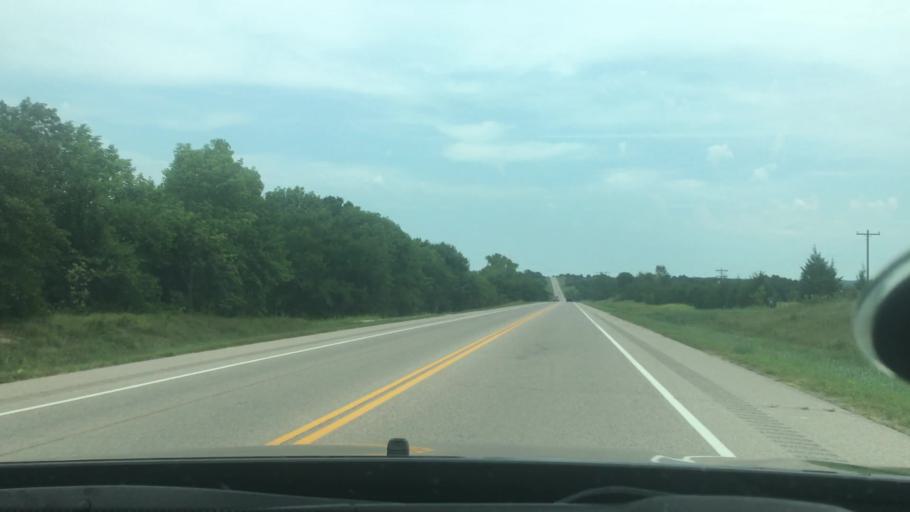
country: US
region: Oklahoma
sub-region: Seminole County
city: Konawa
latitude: 35.0170
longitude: -96.6784
